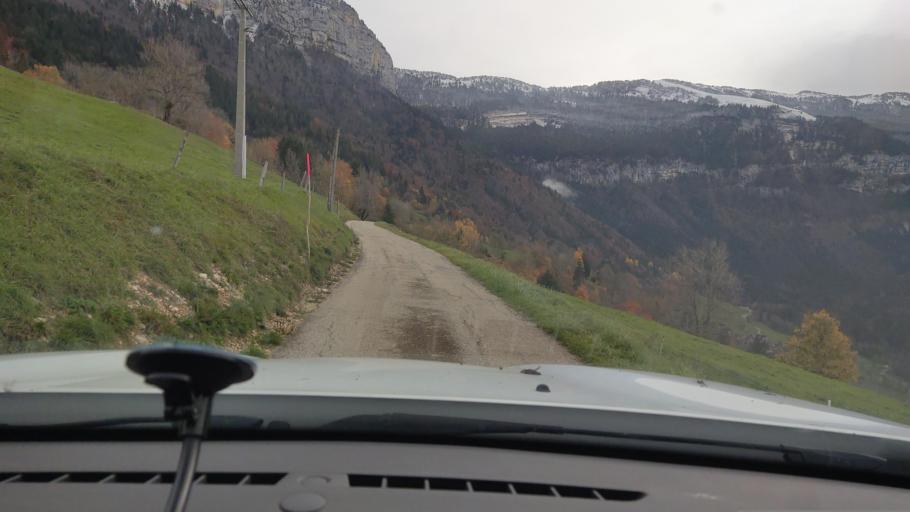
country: FR
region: Rhone-Alpes
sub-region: Departement de l'Isere
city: Saint-Vincent-de-Mercuze
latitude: 45.4137
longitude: 5.8778
